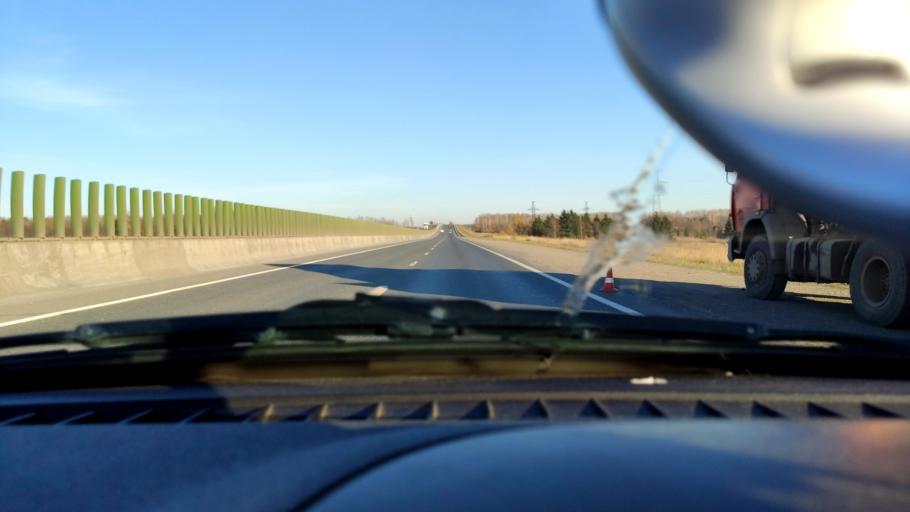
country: RU
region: Perm
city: Froly
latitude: 57.9321
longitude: 56.2809
